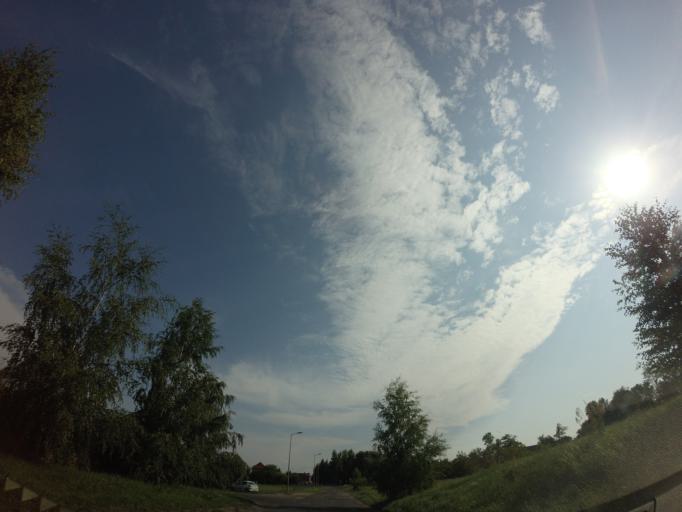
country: PL
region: West Pomeranian Voivodeship
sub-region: Powiat stargardzki
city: Stargard Szczecinski
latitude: 53.3006
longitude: 15.0496
